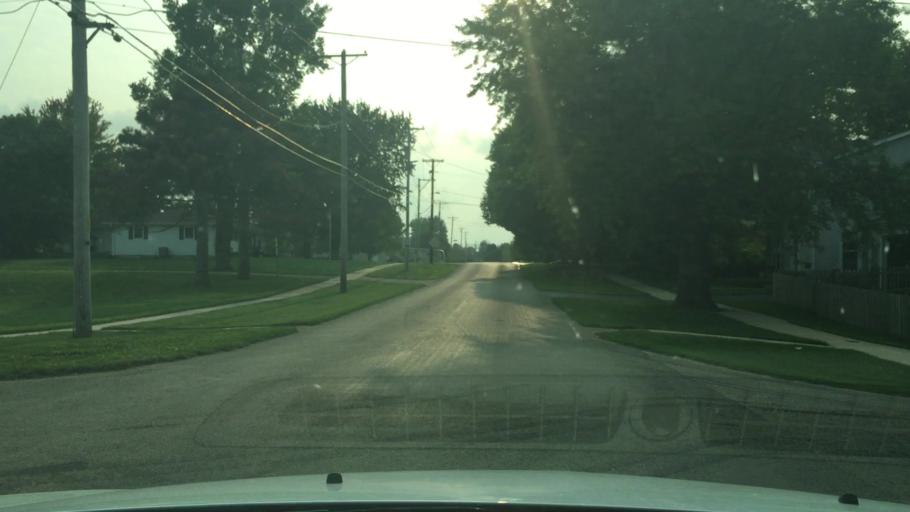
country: US
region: Illinois
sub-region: Ogle County
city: Hillcrest
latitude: 41.9288
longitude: -88.9671
